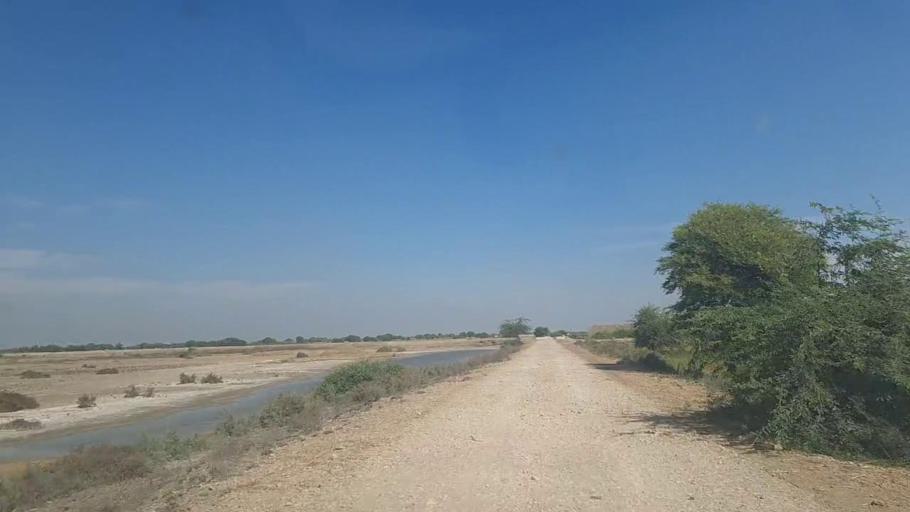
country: PK
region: Sindh
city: Mirpur Batoro
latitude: 24.7059
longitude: 68.2412
